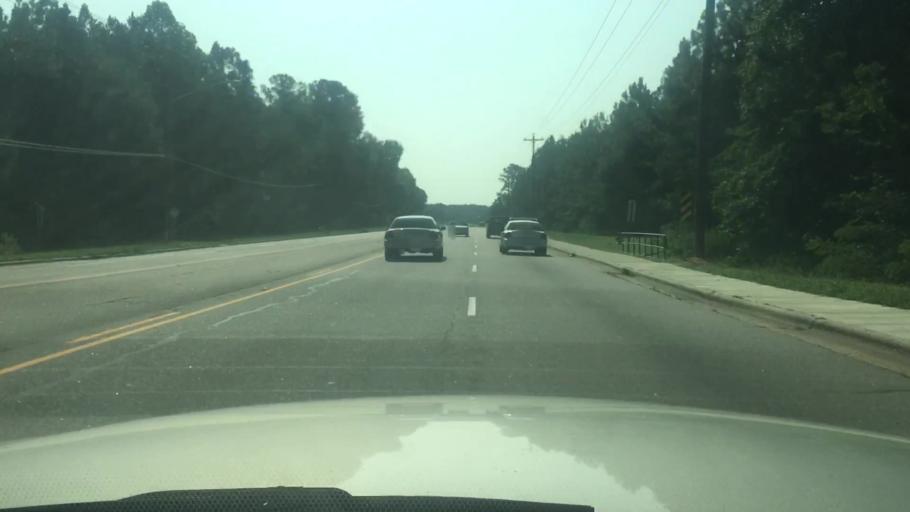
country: US
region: North Carolina
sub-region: Cumberland County
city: Vander
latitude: 35.0113
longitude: -78.8327
